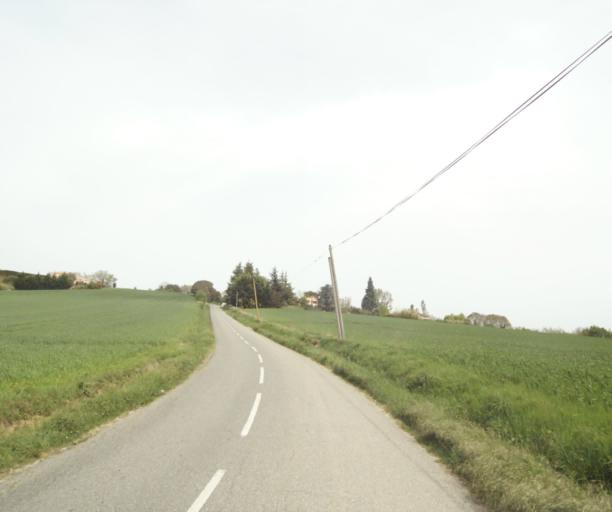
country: FR
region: Midi-Pyrenees
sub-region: Departement de la Haute-Garonne
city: Castanet-Tolosan
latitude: 43.5007
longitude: 1.4850
